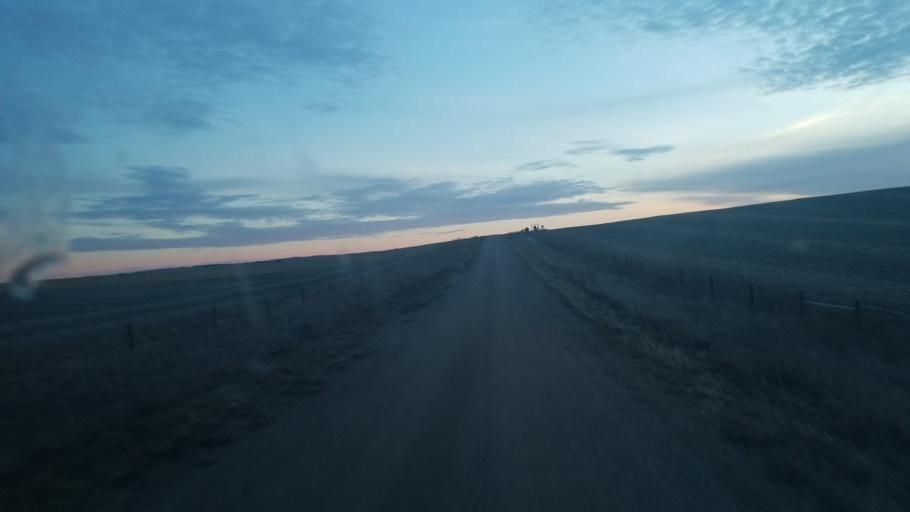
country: US
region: Nebraska
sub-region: Knox County
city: Center
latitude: 42.6465
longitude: -97.7991
